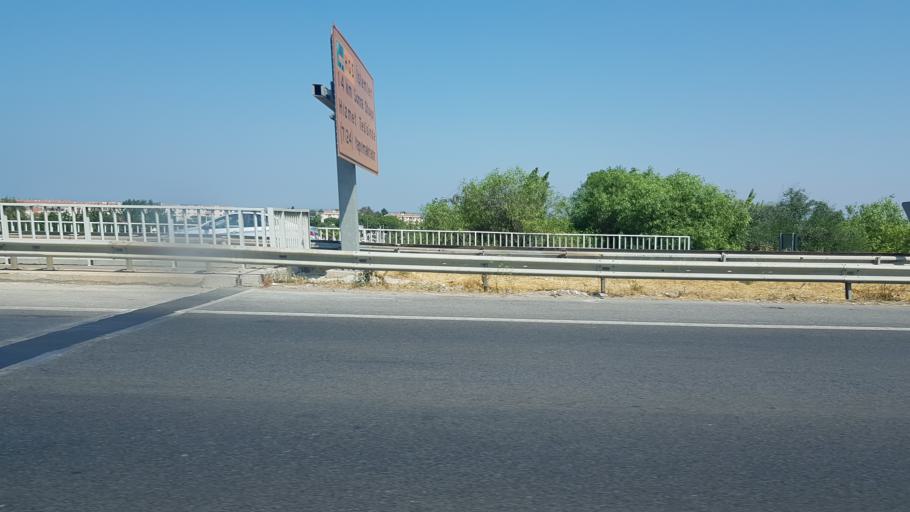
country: TR
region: Izmir
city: Karsiyaka
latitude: 38.3977
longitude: 27.0006
